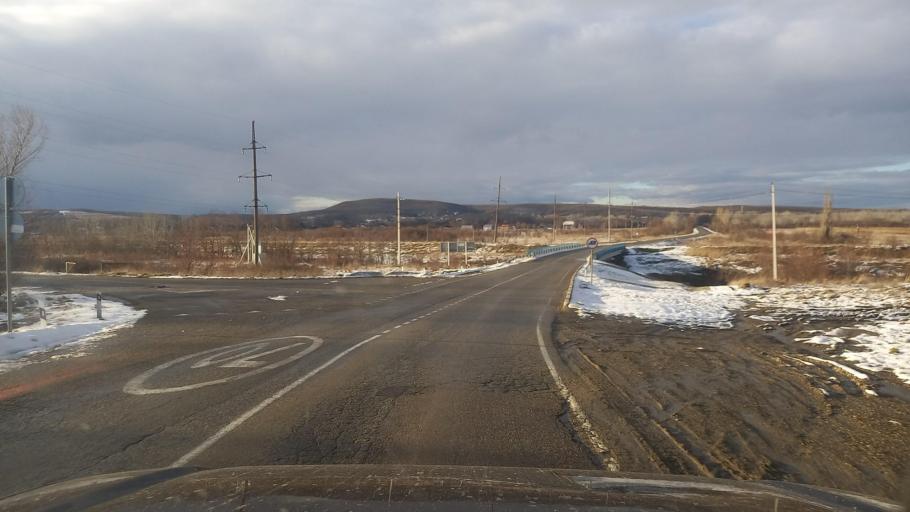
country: RU
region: Krasnodarskiy
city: Smolenskaya
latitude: 44.7719
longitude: 38.8186
